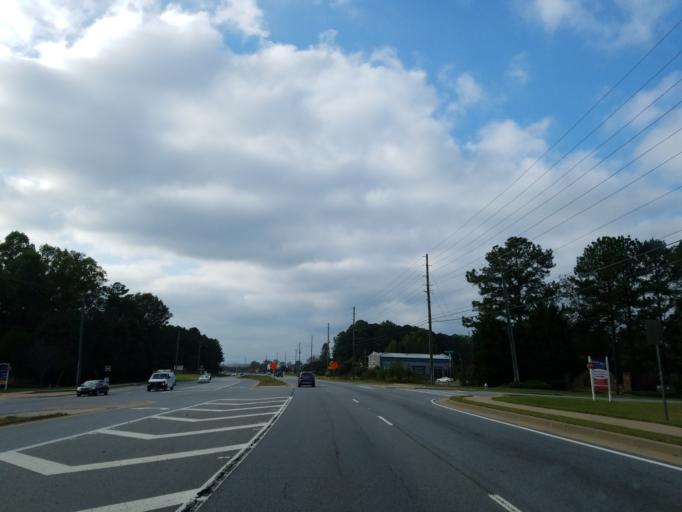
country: US
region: Georgia
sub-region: Cobb County
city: Acworth
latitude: 34.0957
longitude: -84.6236
